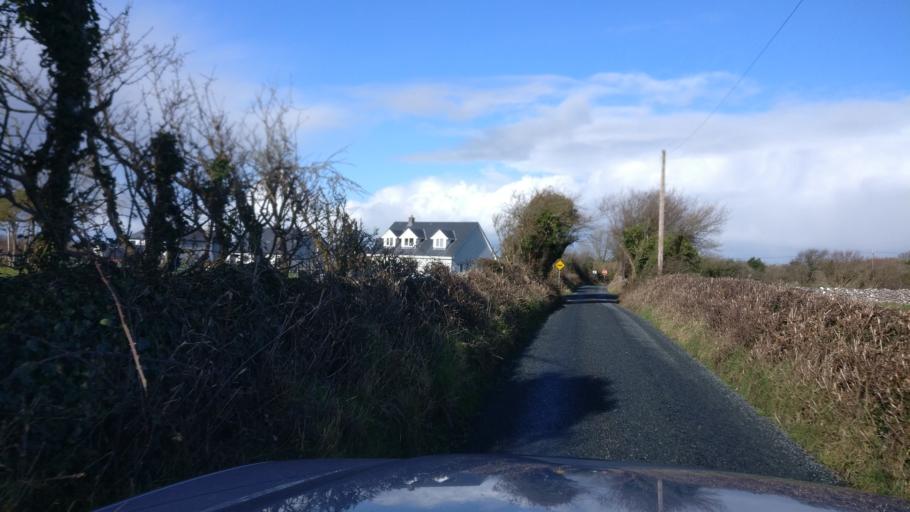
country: IE
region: Connaught
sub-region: County Galway
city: Athenry
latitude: 53.2406
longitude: -8.7756
